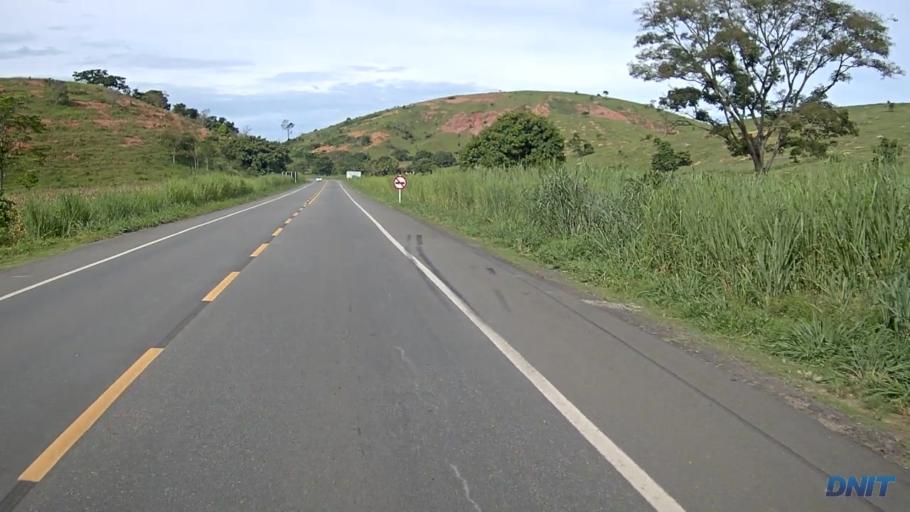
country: BR
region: Minas Gerais
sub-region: Belo Oriente
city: Belo Oriente
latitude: -19.2037
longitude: -42.2930
